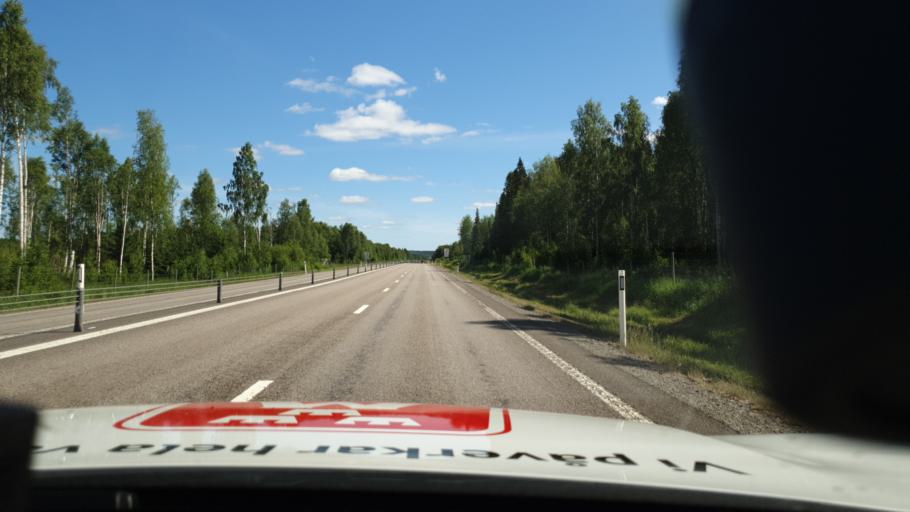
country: SE
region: Norrbotten
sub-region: Kalix Kommun
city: Toere
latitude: 65.8988
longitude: 22.8753
